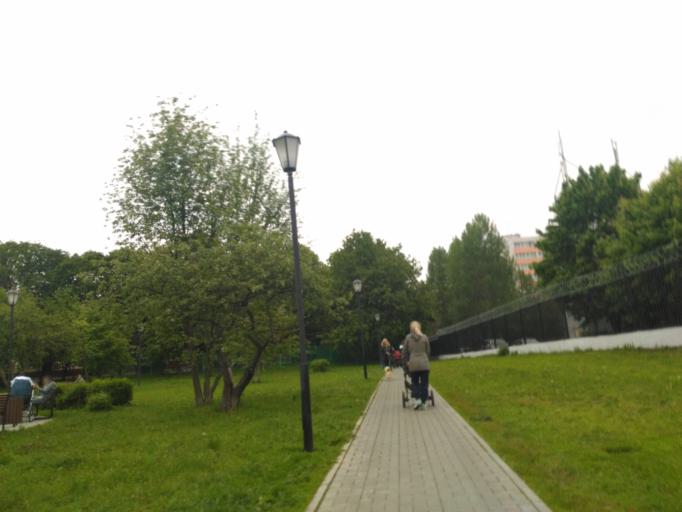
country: RU
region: Moscow
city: Tyoply Stan
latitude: 55.6408
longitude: 37.5176
